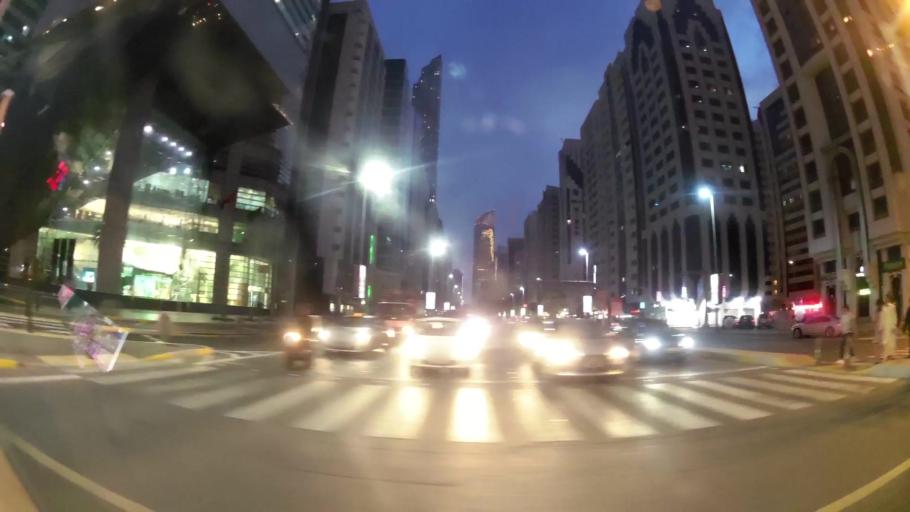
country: AE
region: Abu Dhabi
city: Abu Dhabi
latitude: 24.4921
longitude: 54.3616
